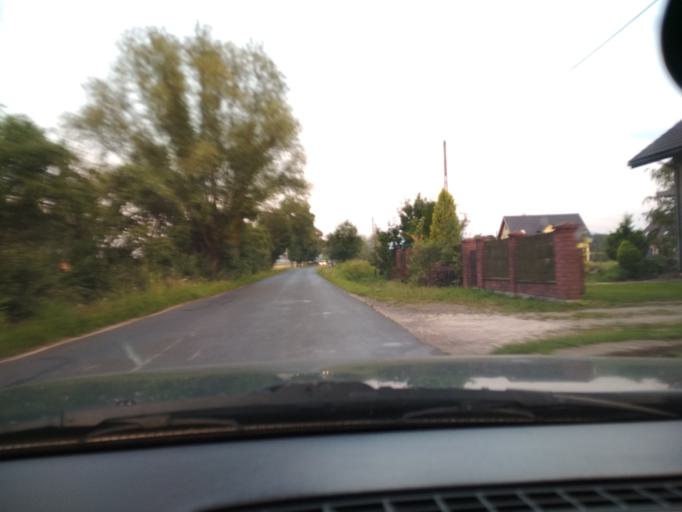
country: PL
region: Silesian Voivodeship
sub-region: Powiat bielski
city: Bronow
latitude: 49.8566
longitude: 18.9191
